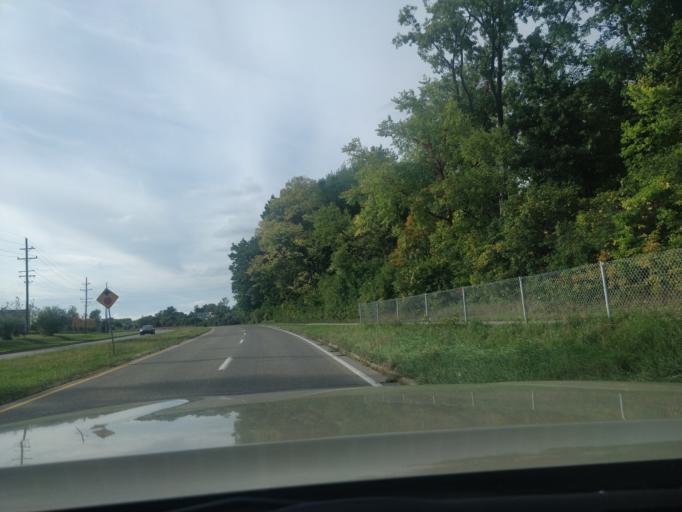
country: US
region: Michigan
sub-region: Wayne County
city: Romulus
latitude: 42.2188
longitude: -83.4205
